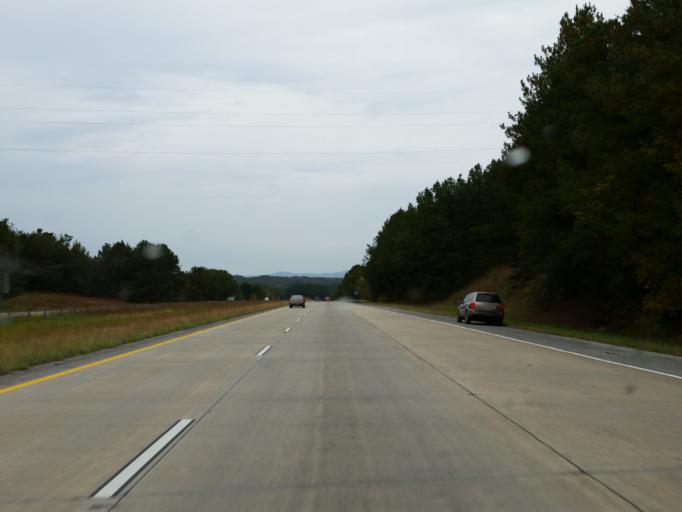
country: US
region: Georgia
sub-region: Cherokee County
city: Ball Ground
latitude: 34.3328
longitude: -84.3931
